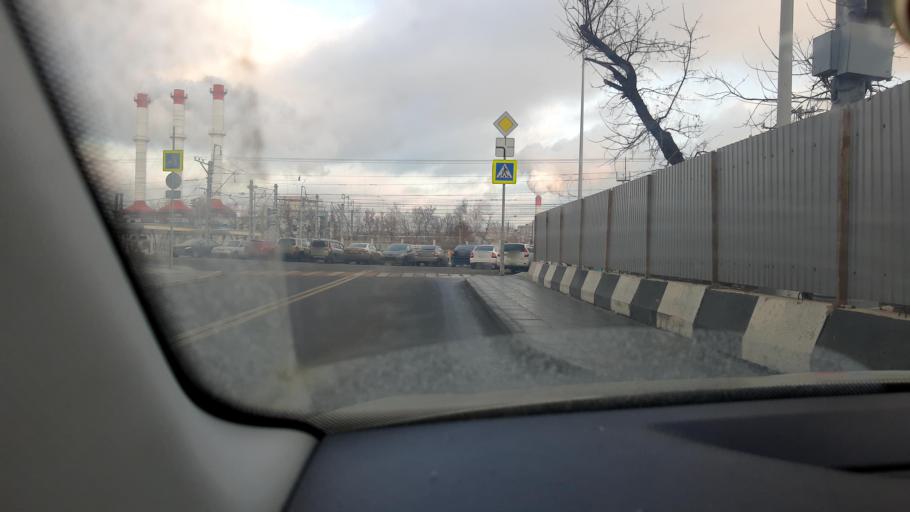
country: RU
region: Moscow
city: Tekstil'shchiki
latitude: 55.7322
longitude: 37.7329
